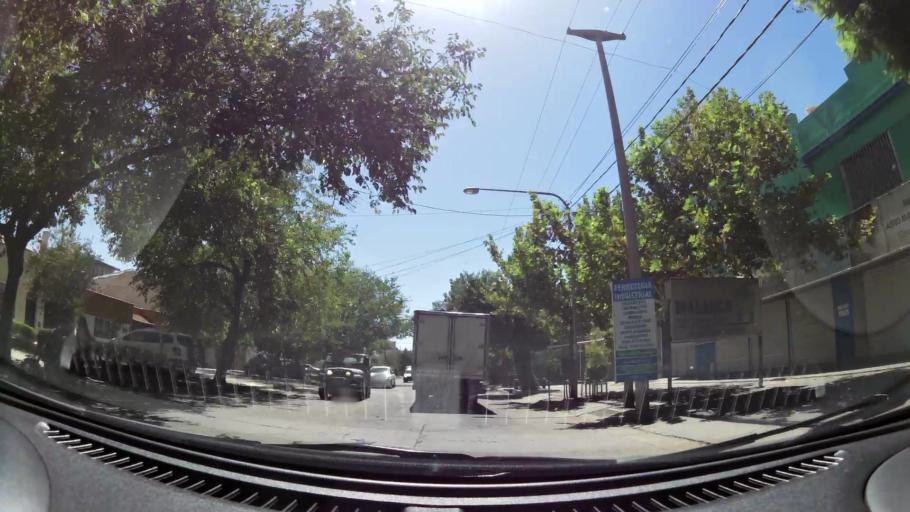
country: AR
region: Mendoza
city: Mendoza
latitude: -32.8806
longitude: -68.8134
